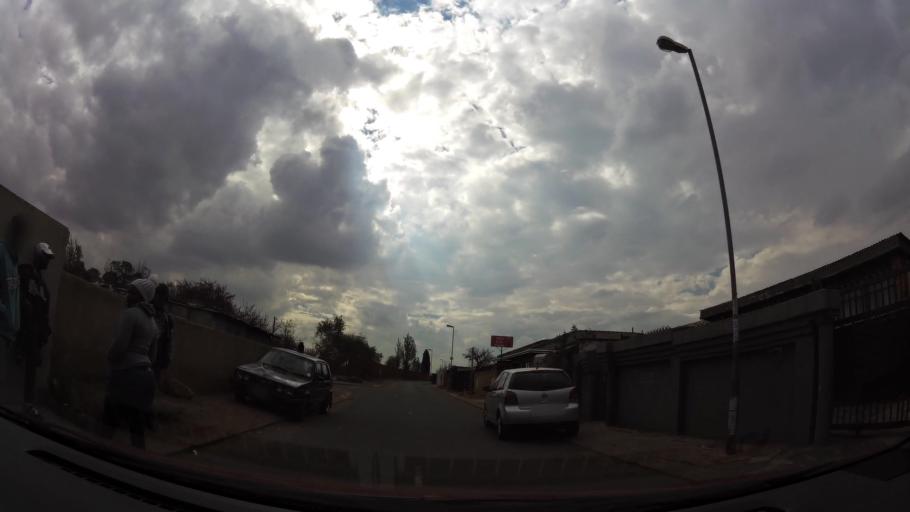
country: ZA
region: Gauteng
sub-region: City of Johannesburg Metropolitan Municipality
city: Soweto
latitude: -26.2511
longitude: 27.8529
